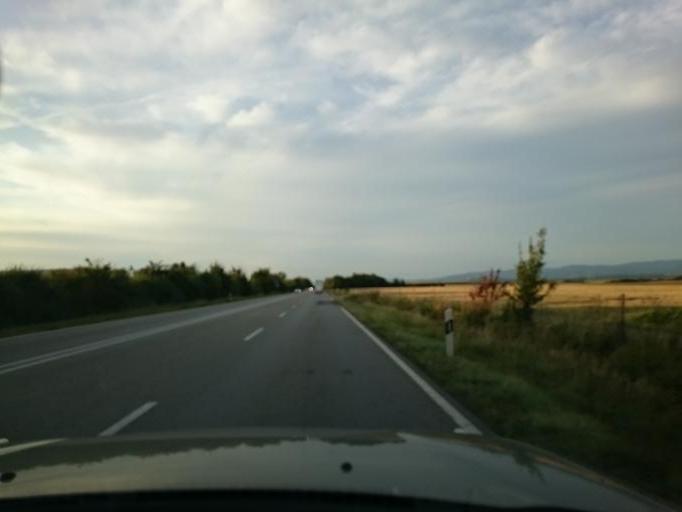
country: DE
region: Bavaria
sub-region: Lower Bavaria
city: Oberschneiding
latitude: 48.7818
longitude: 12.6502
